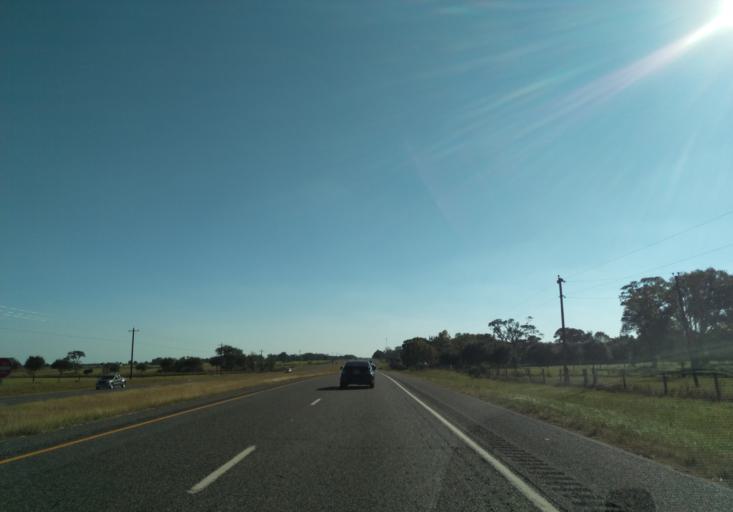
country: US
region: Texas
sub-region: Waller County
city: Hempstead
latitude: 30.1506
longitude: -96.0697
